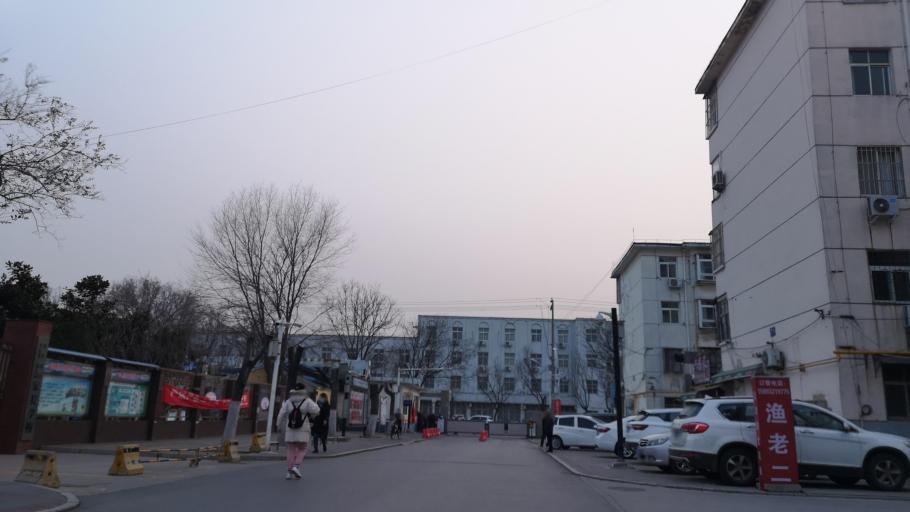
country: CN
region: Henan Sheng
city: Zhongyuanlu
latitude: 35.7809
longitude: 115.0746
